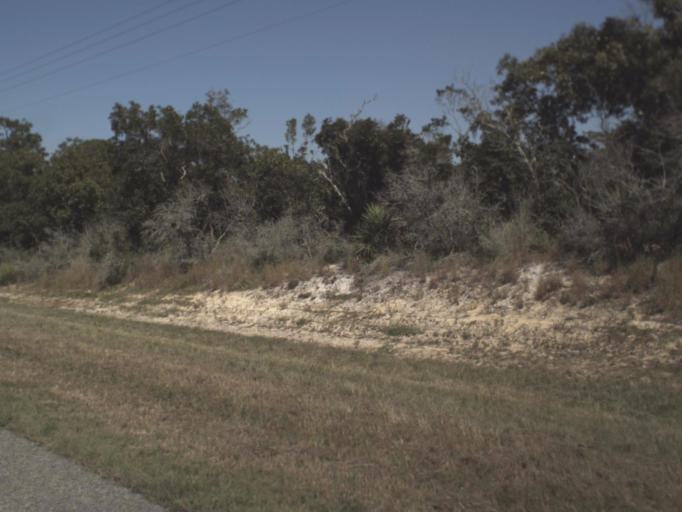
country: US
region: Florida
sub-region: Highlands County
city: Lake Placid
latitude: 27.2270
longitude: -81.3285
